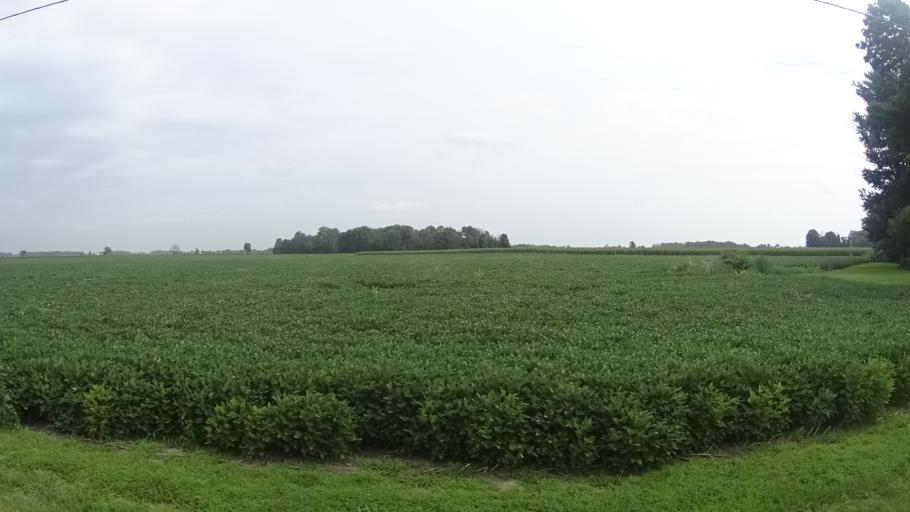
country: US
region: Indiana
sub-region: Madison County
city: Pendleton
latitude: 40.0347
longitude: -85.7947
